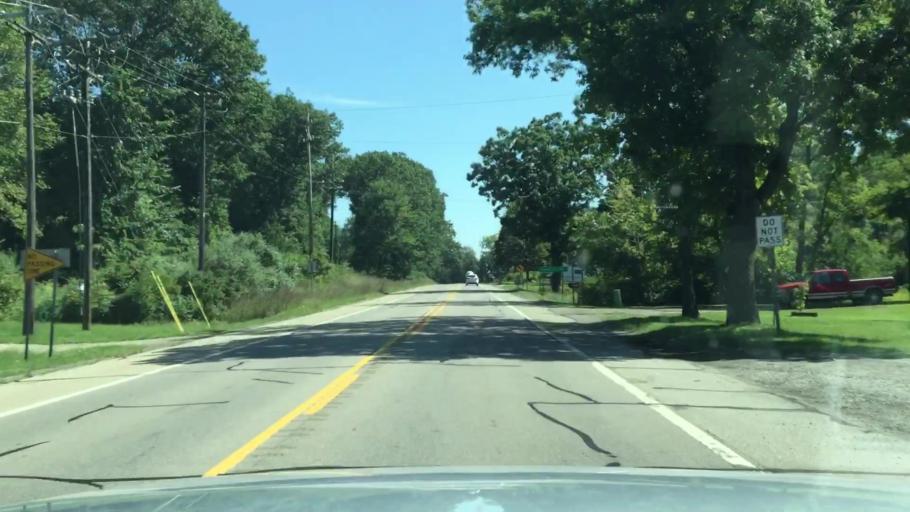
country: US
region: Michigan
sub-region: Jackson County
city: Brooklyn
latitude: 42.0593
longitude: -84.1307
